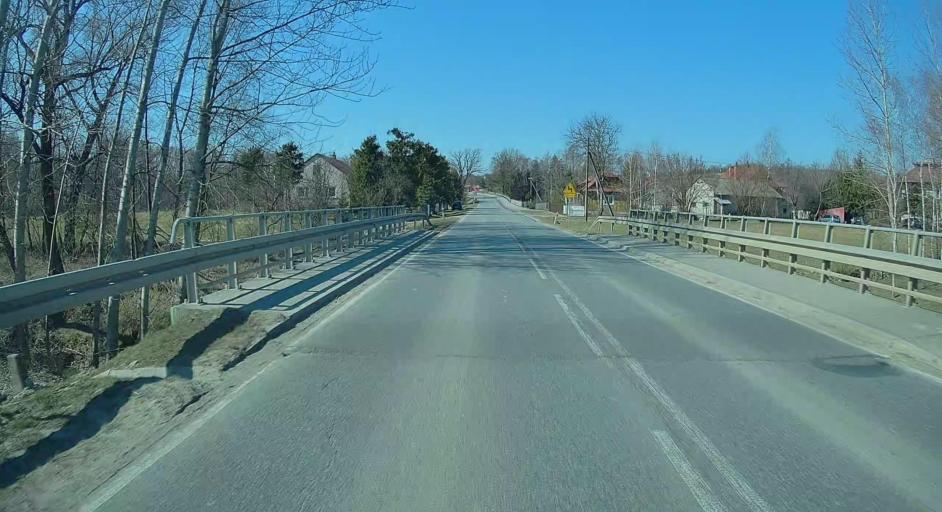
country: PL
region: Subcarpathian Voivodeship
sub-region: Powiat rzeszowski
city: Tyczyn
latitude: 49.9650
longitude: 22.0793
